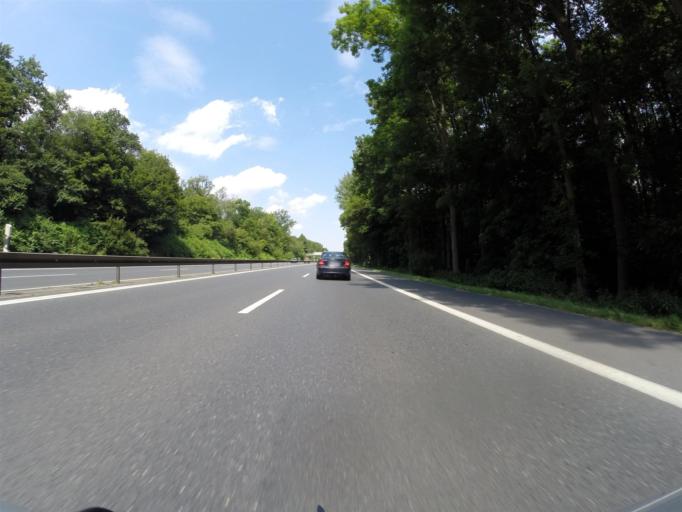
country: DE
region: Lower Saxony
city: Laatzen
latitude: 52.3391
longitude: 9.8037
